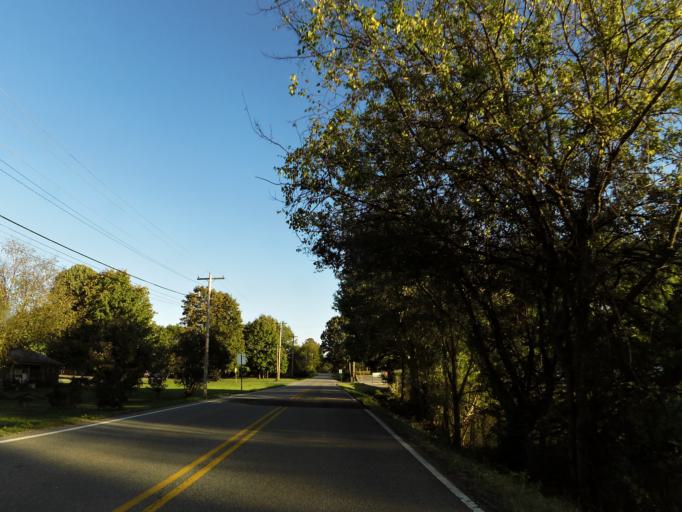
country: US
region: Tennessee
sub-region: Blount County
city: Eagleton Village
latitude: 35.8351
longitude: -83.9570
